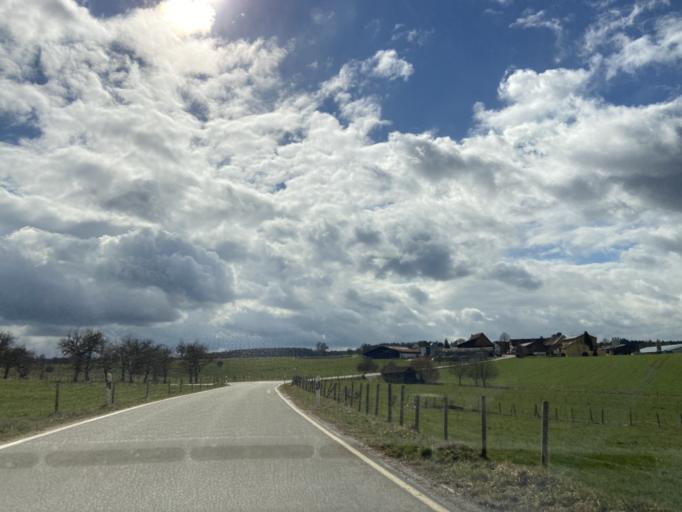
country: DE
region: Baden-Wuerttemberg
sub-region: Tuebingen Region
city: Pfullendorf
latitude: 47.9678
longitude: 9.3138
